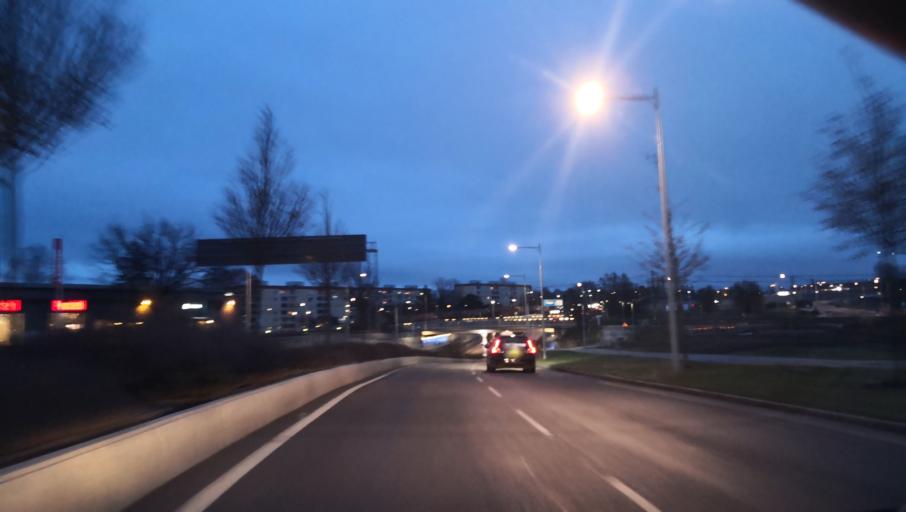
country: SE
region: Stockholm
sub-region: Taby Kommun
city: Taby
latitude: 59.4486
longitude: 18.0916
